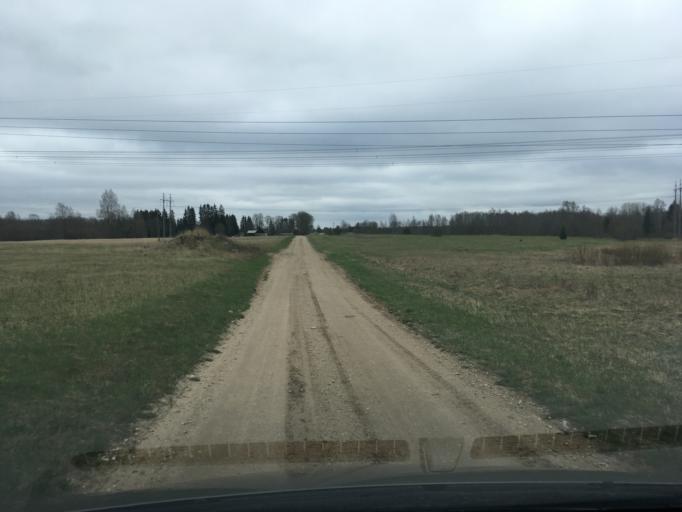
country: EE
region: Harju
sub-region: Raasiku vald
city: Arukula
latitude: 59.2734
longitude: 25.1173
